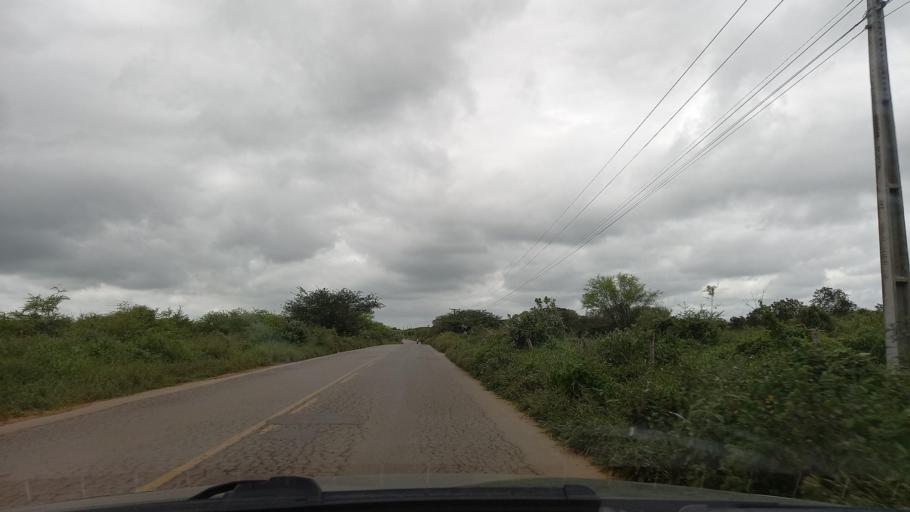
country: BR
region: Sergipe
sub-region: Caninde De Sao Francisco
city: Caninde de Sao Francisco
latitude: -9.6871
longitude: -37.7856
